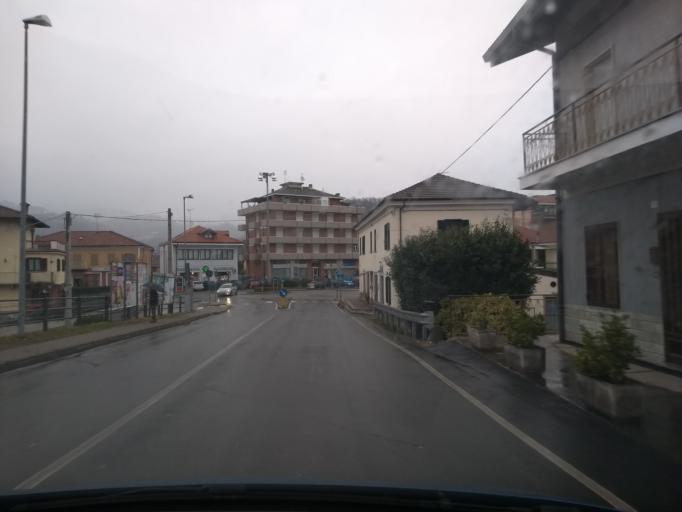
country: IT
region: Piedmont
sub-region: Provincia di Torino
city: Cuorgne
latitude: 45.3958
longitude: 7.6550
